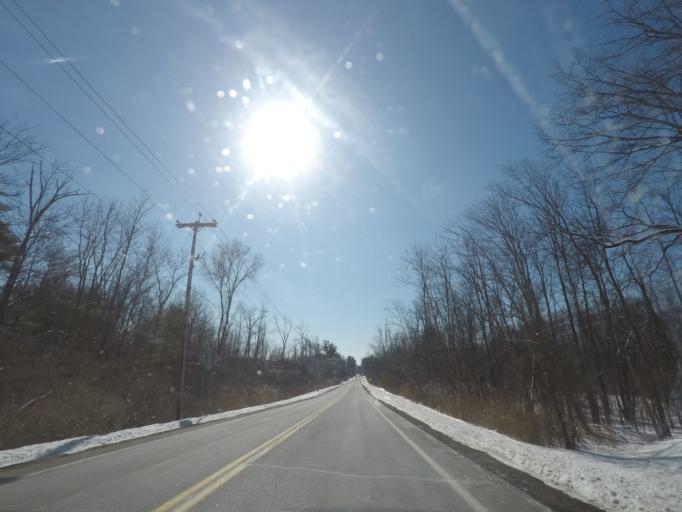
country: US
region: New York
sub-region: Saratoga County
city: Country Knolls
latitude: 42.9340
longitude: -73.8250
